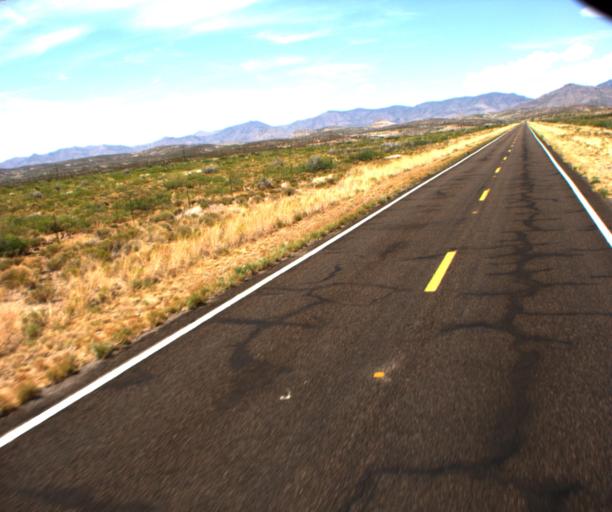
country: US
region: Arizona
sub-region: Greenlee County
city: Clifton
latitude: 32.9718
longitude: -109.2008
